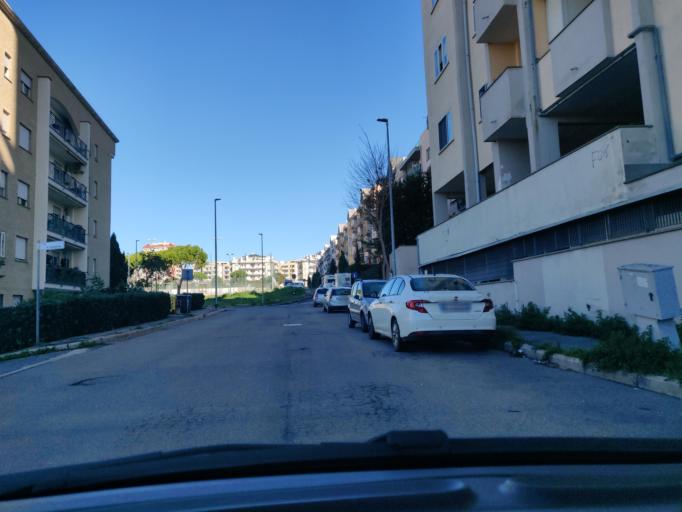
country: IT
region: Latium
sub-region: Citta metropolitana di Roma Capitale
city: Civitavecchia
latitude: 42.0964
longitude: 11.8222
